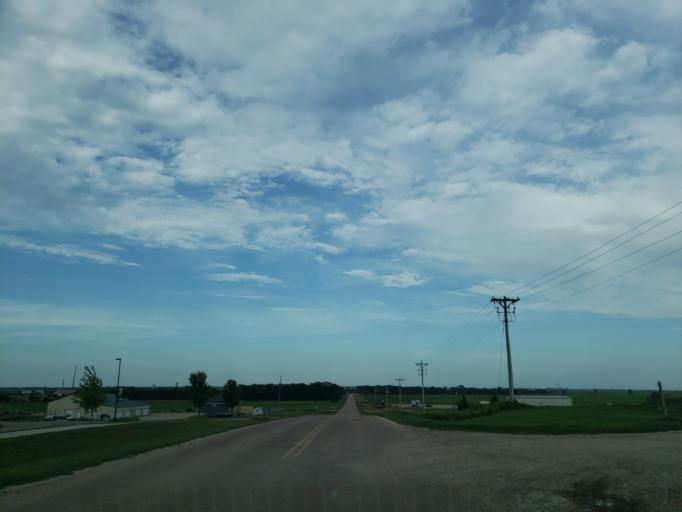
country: US
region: South Dakota
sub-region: Davison County
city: Mitchell
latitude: 43.6877
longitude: -98.0001
